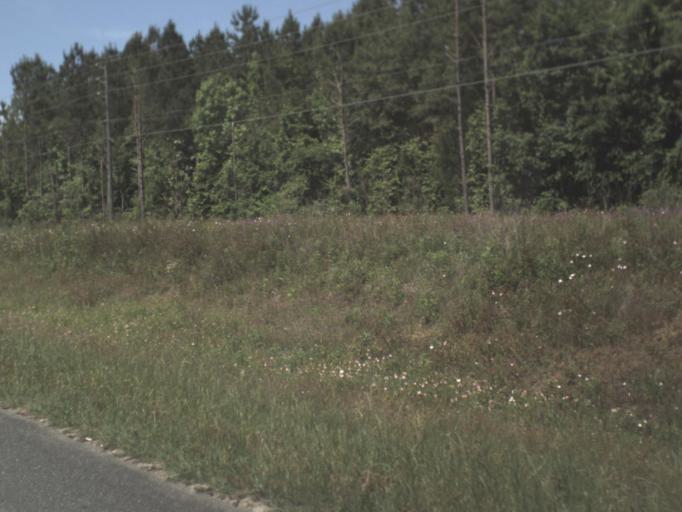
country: US
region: Florida
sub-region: Jackson County
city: Marianna
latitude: 30.7988
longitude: -85.2150
